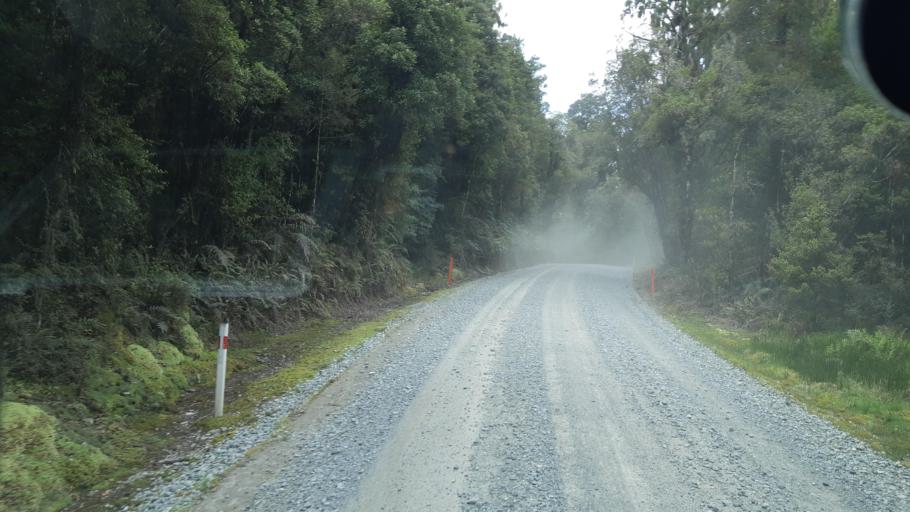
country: NZ
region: West Coast
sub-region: Grey District
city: Greymouth
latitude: -42.7244
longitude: 171.2384
